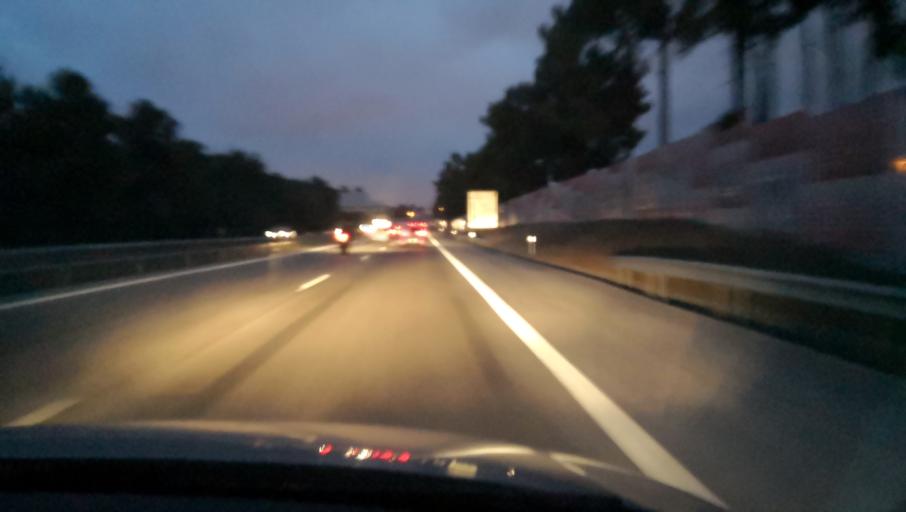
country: PT
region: Setubal
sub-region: Barreiro
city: Santo Antonio da Charneca
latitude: 38.6134
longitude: -9.0270
